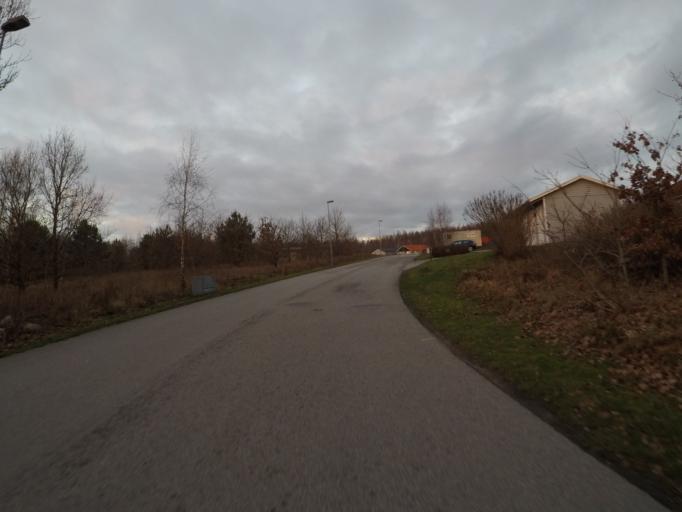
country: SE
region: Skane
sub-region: Sjobo Kommun
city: Sjoebo
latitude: 55.6436
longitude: 13.6949
